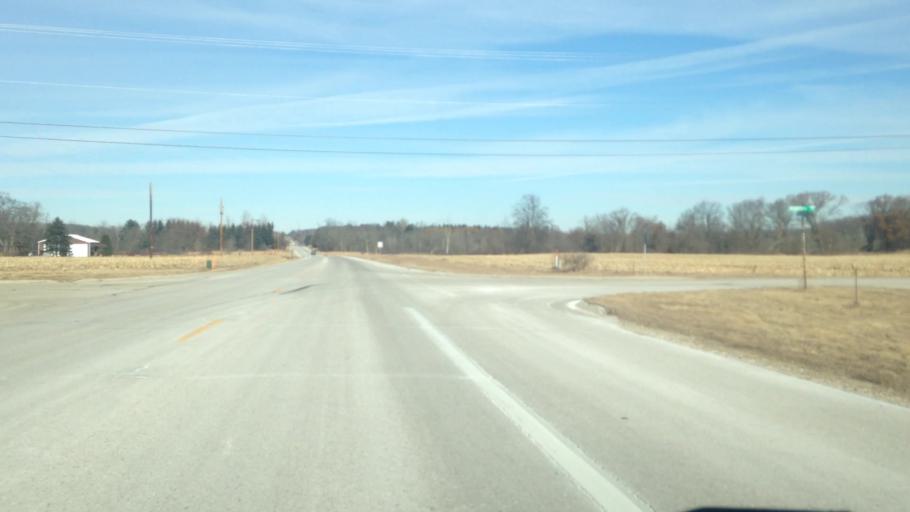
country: US
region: Wisconsin
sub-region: Washington County
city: Slinger
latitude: 43.2808
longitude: -88.2612
